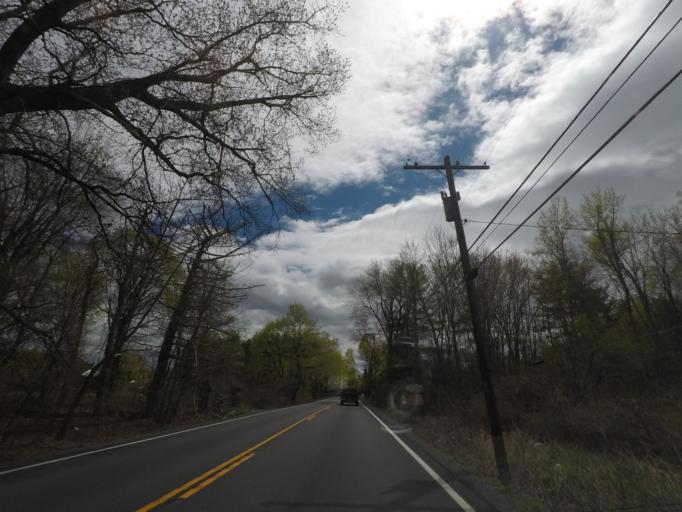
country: US
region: New York
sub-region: Rensselaer County
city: Castleton-on-Hudson
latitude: 42.5227
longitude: -73.7876
